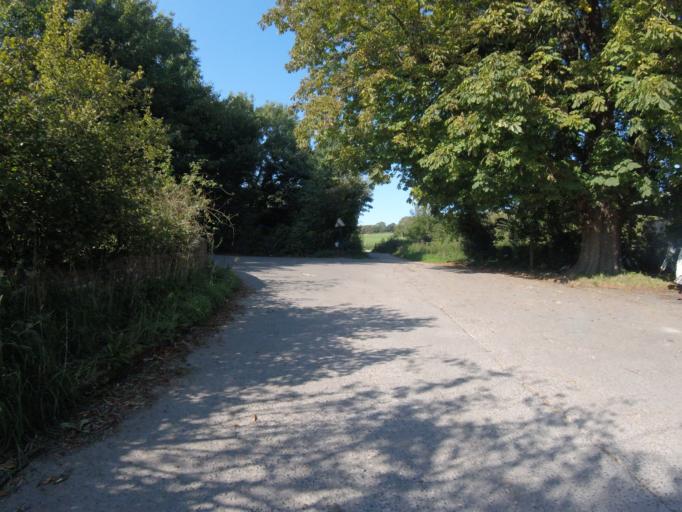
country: GB
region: England
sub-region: Brighton and Hove
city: Brighton
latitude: 50.8729
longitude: -0.1019
